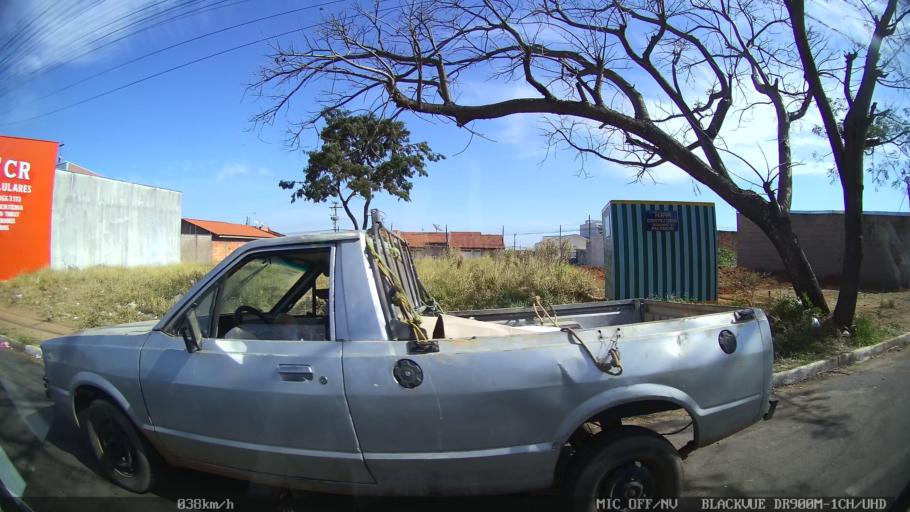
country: BR
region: Sao Paulo
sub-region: Franca
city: Franca
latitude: -20.4825
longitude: -47.4026
